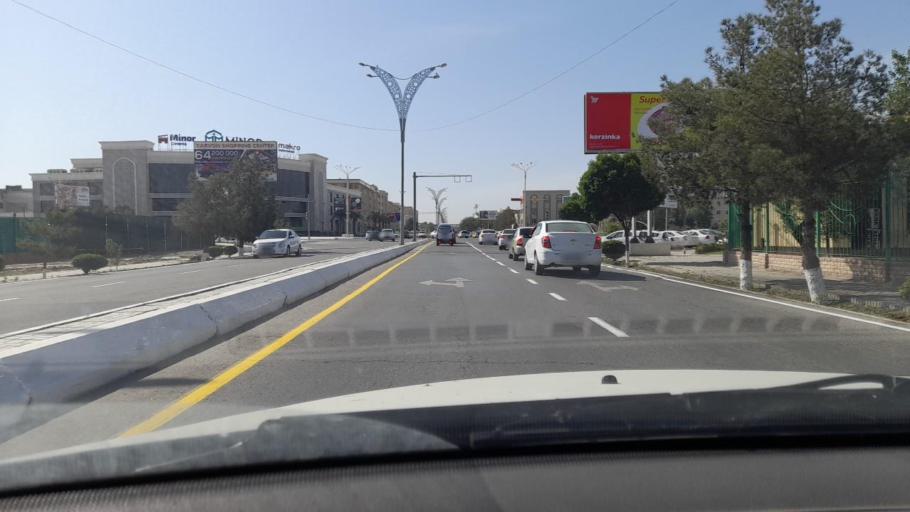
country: UZ
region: Bukhara
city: Bukhara
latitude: 39.7821
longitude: 64.4295
